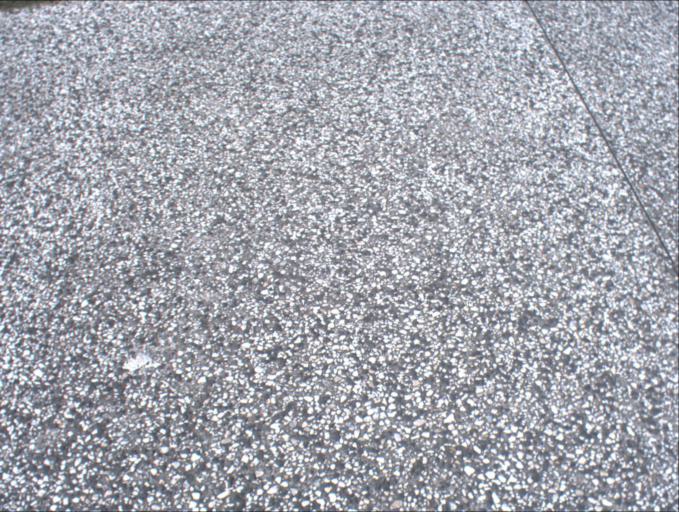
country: AU
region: Queensland
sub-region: Logan
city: Waterford West
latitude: -27.7166
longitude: 153.1434
